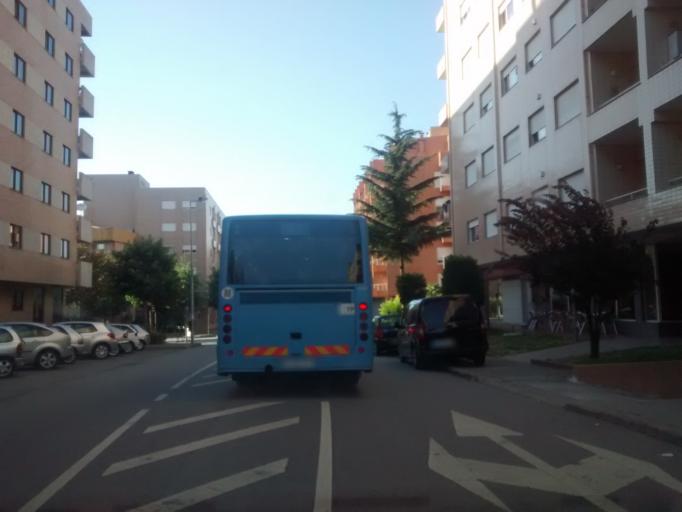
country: PT
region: Braga
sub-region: Braga
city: Braga
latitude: 41.5444
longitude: -8.4020
